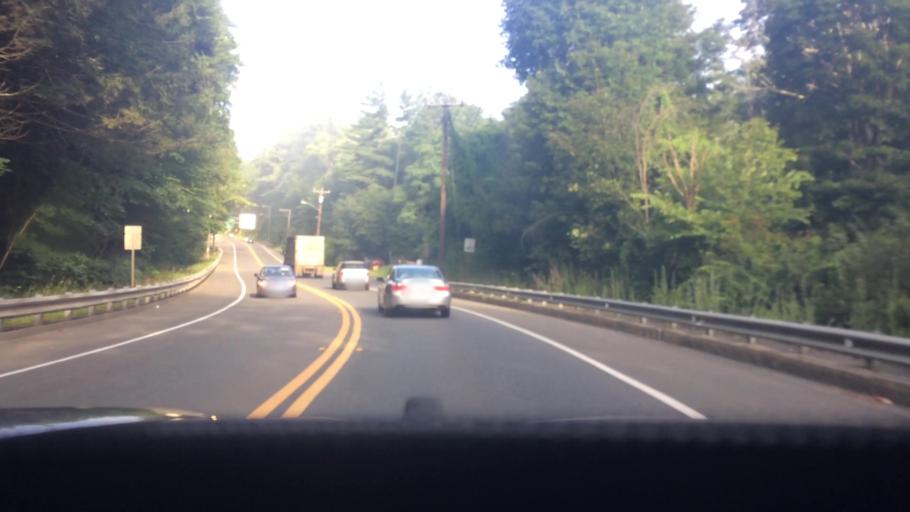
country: US
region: Massachusetts
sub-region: Franklin County
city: Turners Falls
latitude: 42.6169
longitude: -72.5533
